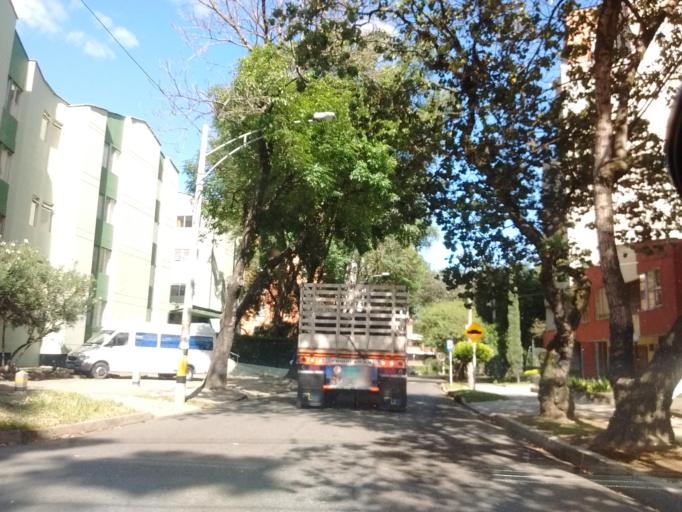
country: CO
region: Antioquia
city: Medellin
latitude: 6.2688
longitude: -75.5931
